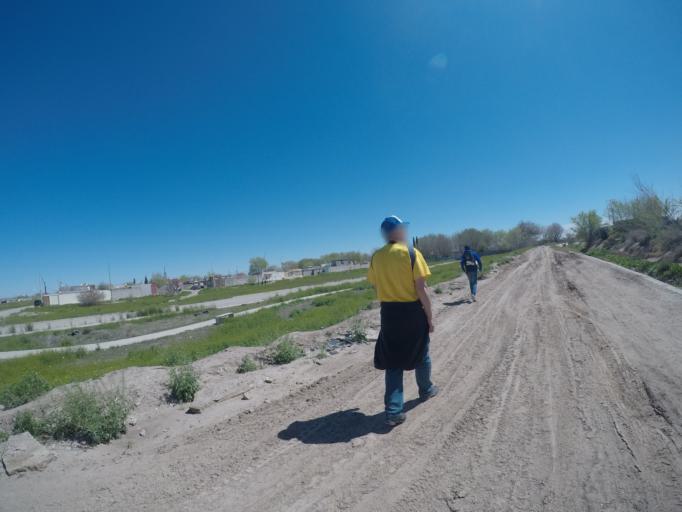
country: US
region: Texas
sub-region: El Paso County
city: Socorro Mission Number 1 Colonia
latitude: 31.6167
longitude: -106.3188
